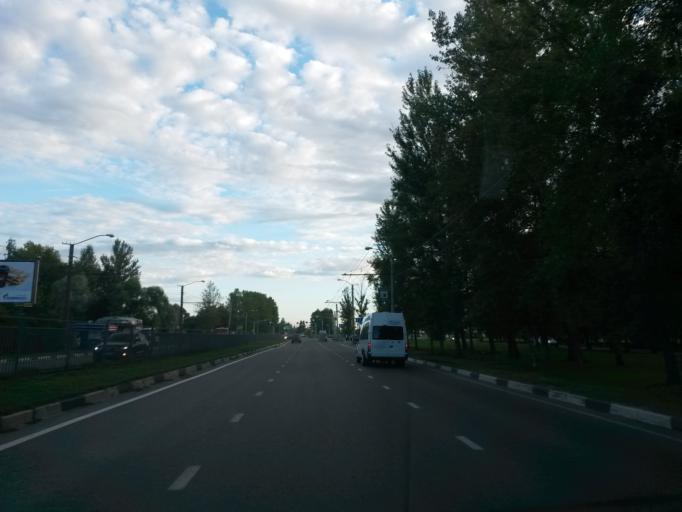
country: RU
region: Jaroslavl
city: Yaroslavl
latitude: 57.6762
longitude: 39.7752
